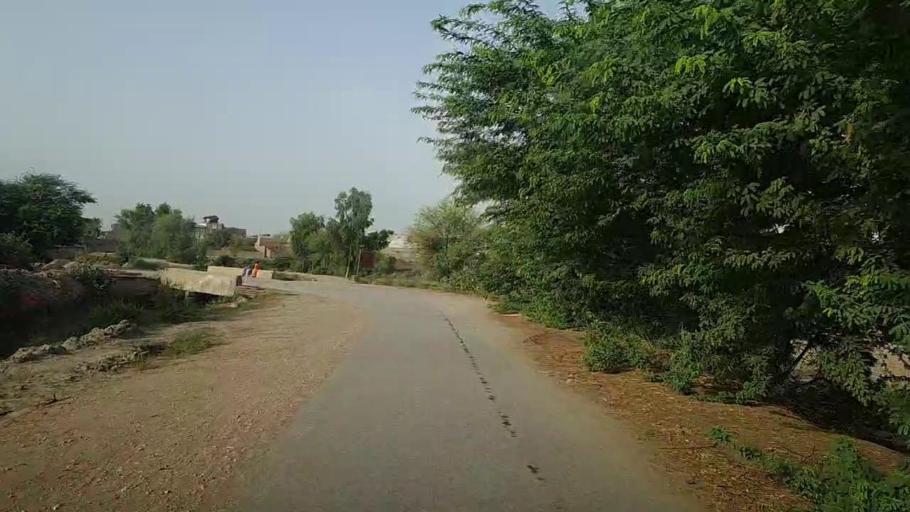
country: PK
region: Sindh
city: Khairpur Nathan Shah
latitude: 27.1166
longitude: 67.7884
